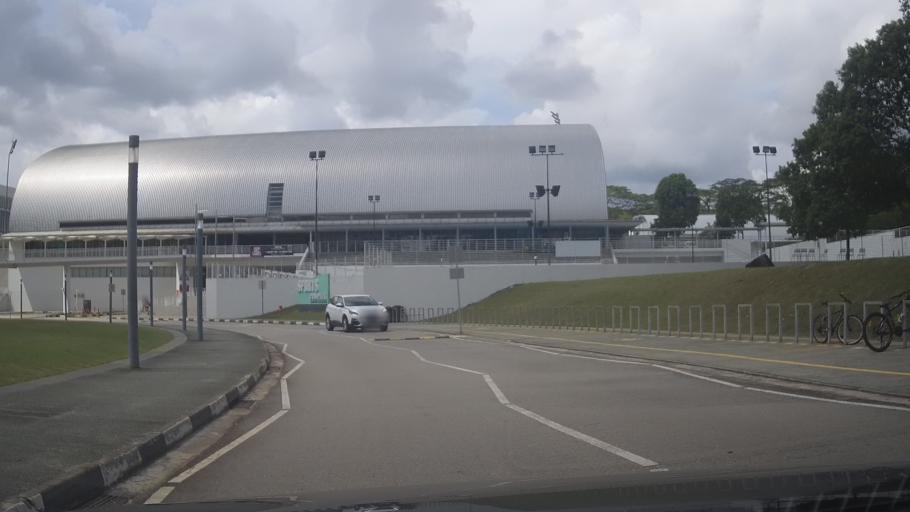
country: MY
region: Johor
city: Johor Bahru
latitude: 1.4458
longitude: 103.7847
